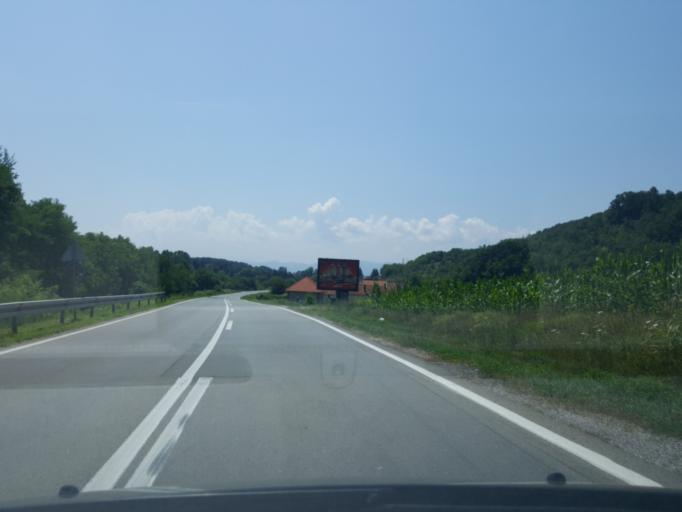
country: RS
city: Prislonica
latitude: 43.9774
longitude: 20.4194
